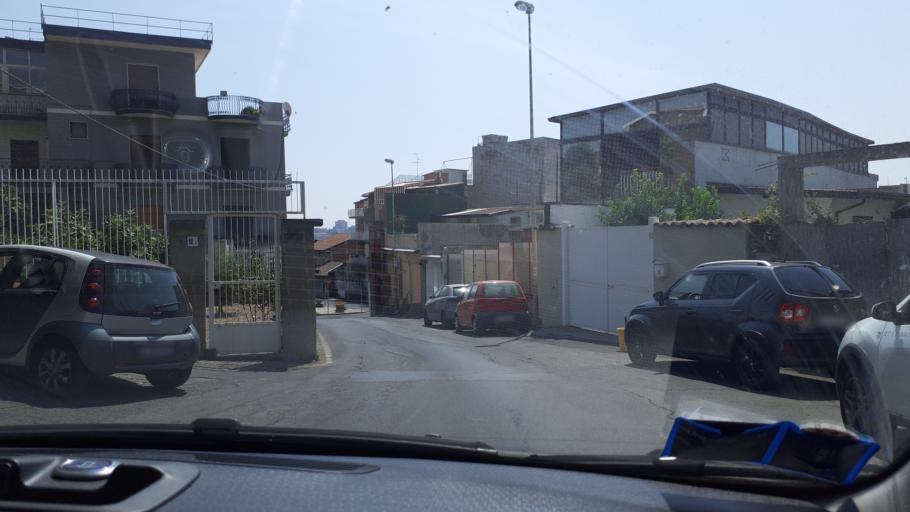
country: IT
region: Sicily
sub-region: Catania
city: Misterbianco
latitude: 37.5168
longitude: 15.0183
